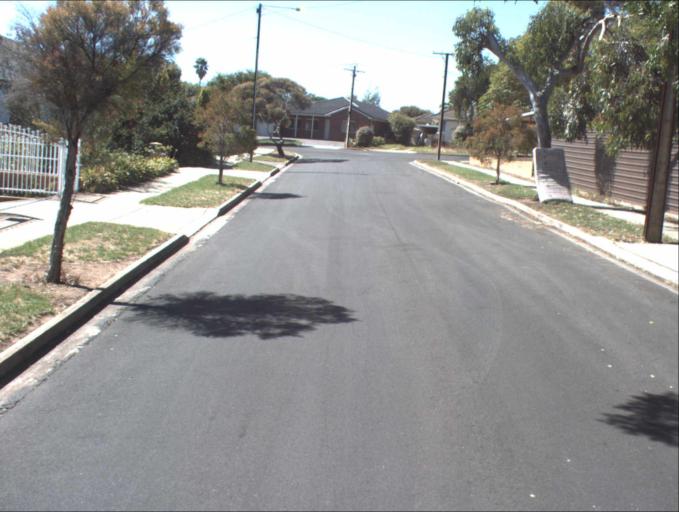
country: AU
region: South Australia
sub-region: Port Adelaide Enfield
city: Blair Athol
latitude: -34.8630
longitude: 138.6047
